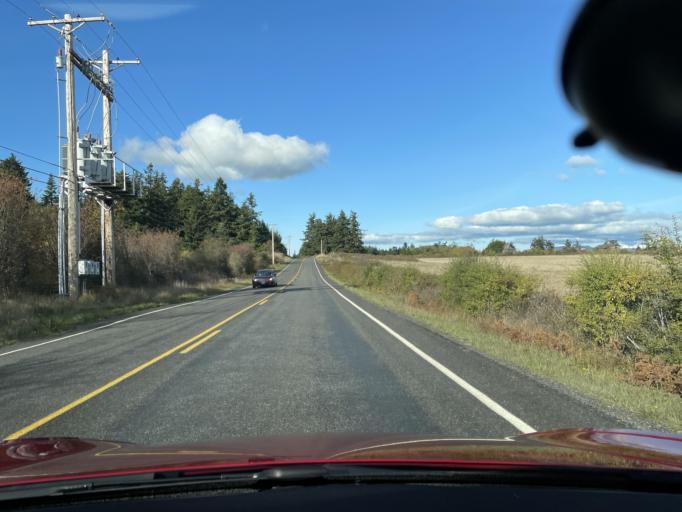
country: US
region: Washington
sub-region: San Juan County
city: Friday Harbor
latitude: 48.4753
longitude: -123.0327
